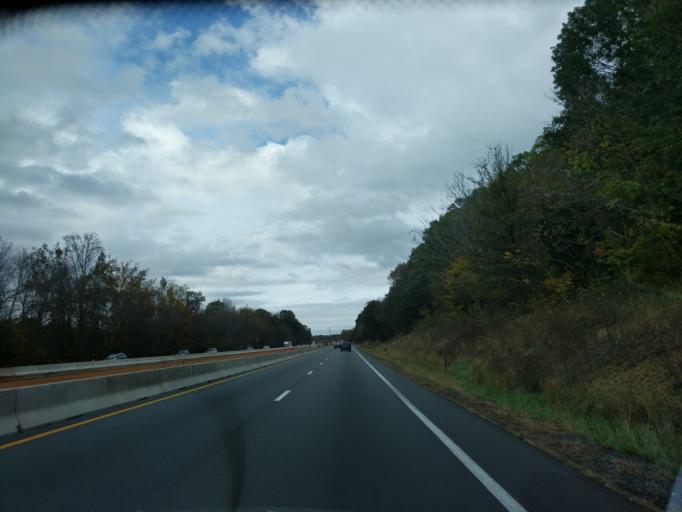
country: US
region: North Carolina
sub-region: Rowan County
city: China Grove
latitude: 35.5634
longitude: -80.5648
